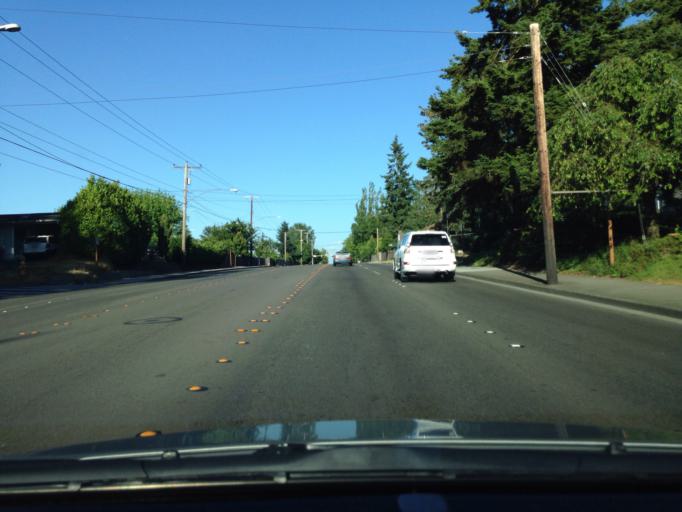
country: US
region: Washington
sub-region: King County
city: SeaTac
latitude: 47.4345
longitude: -122.2923
